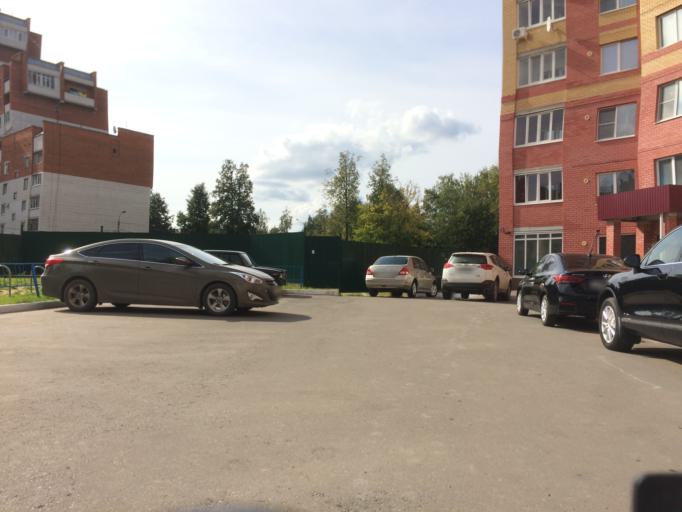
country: RU
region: Mariy-El
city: Yoshkar-Ola
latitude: 56.6383
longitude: 47.8703
